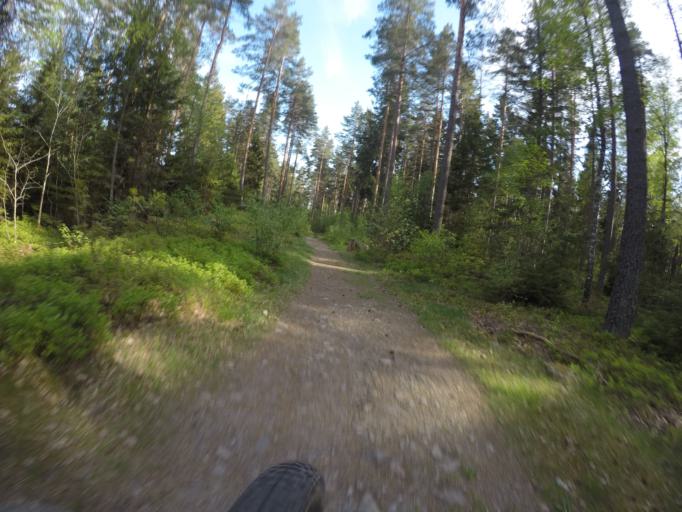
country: SE
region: Vaestmanland
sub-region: Vasteras
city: Vasteras
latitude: 59.6544
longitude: 16.5238
